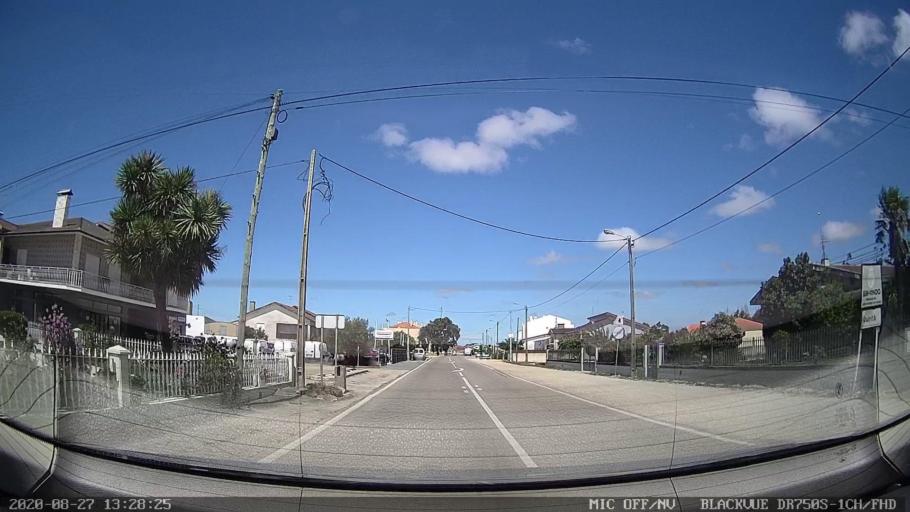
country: PT
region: Aveiro
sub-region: Vagos
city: Vagos
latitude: 40.5205
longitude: -8.6791
